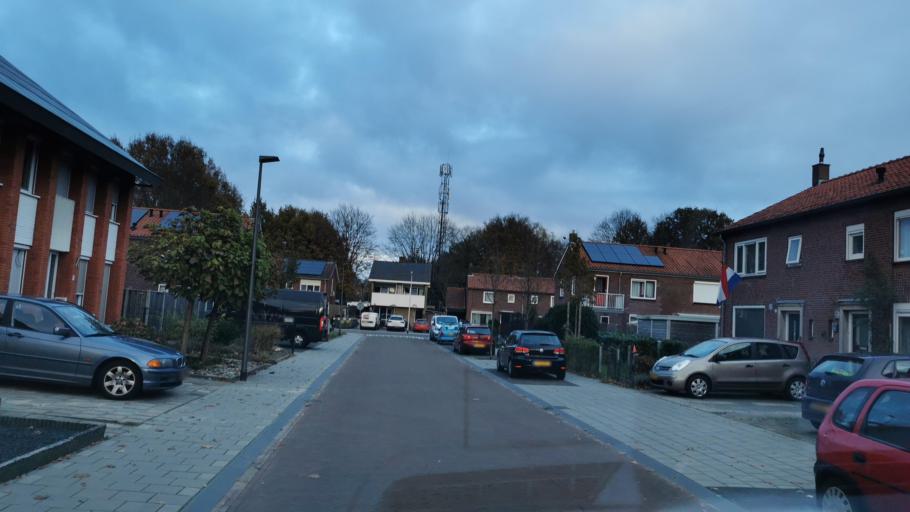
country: DE
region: North Rhine-Westphalia
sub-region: Regierungsbezirk Munster
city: Gronau
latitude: 52.2395
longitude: 7.0346
